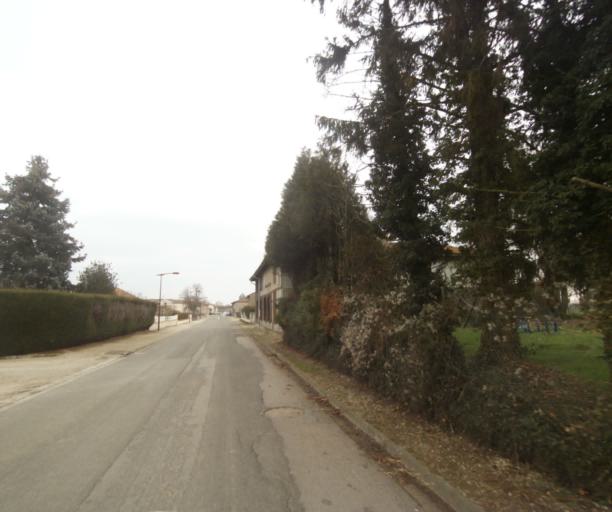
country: FR
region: Champagne-Ardenne
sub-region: Departement de la Marne
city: Pargny-sur-Saulx
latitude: 48.6933
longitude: 4.7983
